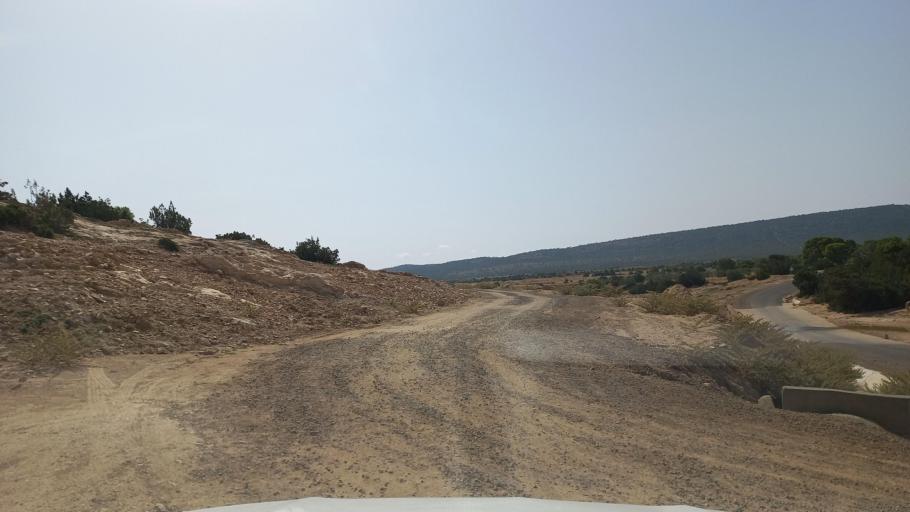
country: TN
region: Al Qasrayn
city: Sbiba
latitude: 35.3978
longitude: 8.9487
